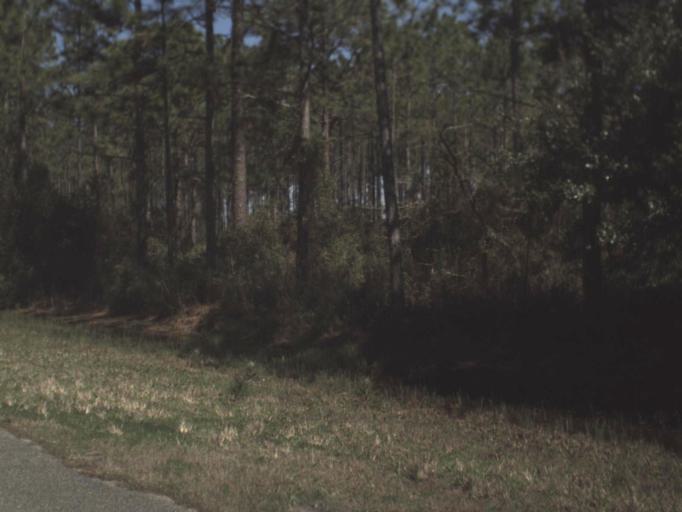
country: US
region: Florida
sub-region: Gulf County
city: Port Saint Joe
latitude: 29.7693
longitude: -85.2638
